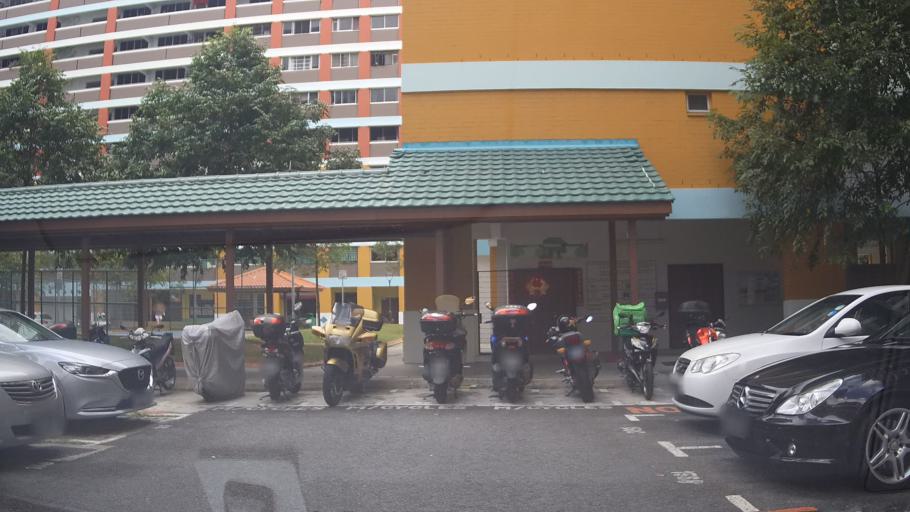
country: SG
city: Singapore
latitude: 1.3477
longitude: 103.9323
